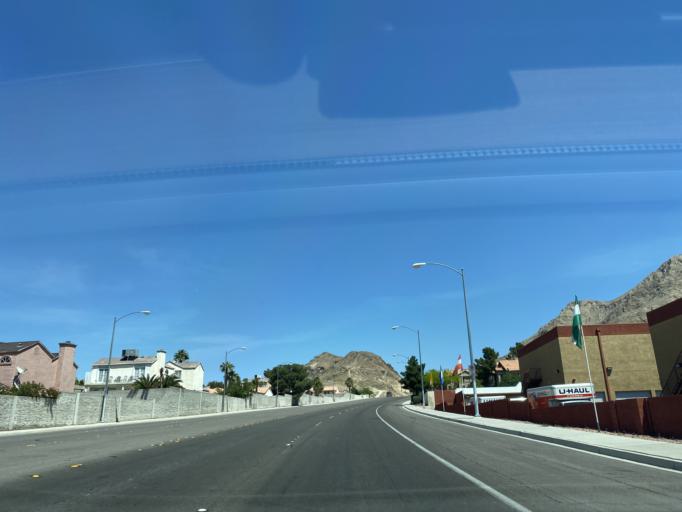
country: US
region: Nevada
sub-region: Clark County
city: Sunrise Manor
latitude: 36.1982
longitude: -115.0165
